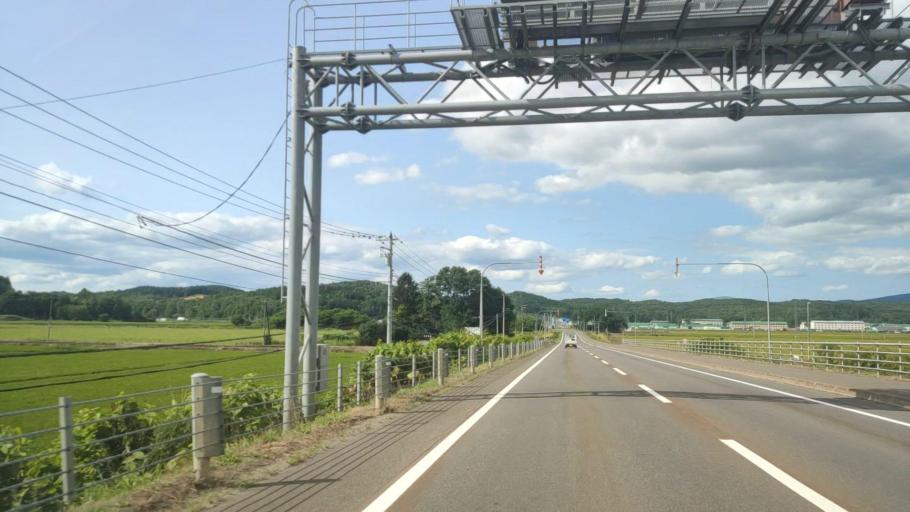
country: JP
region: Hokkaido
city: Nayoro
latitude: 44.3728
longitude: 142.4361
